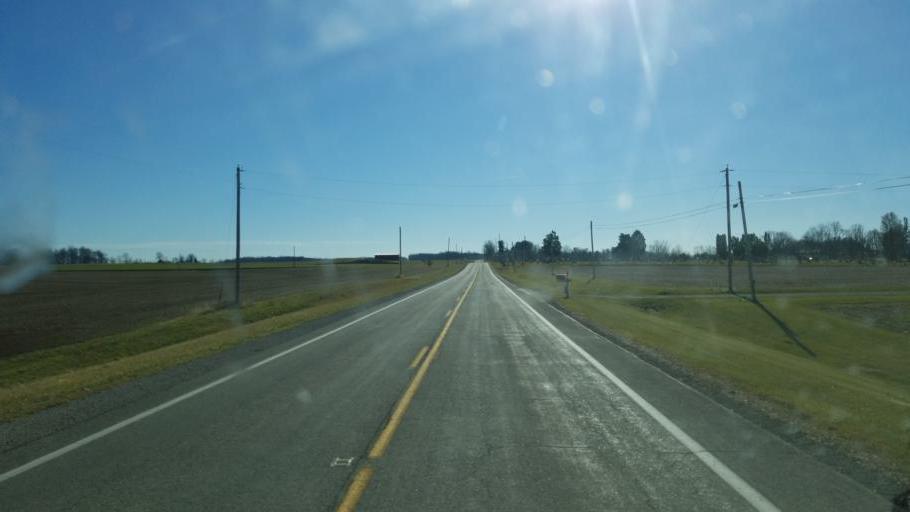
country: US
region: Ohio
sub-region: Crawford County
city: Bucyrus
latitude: 40.8882
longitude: -82.8548
